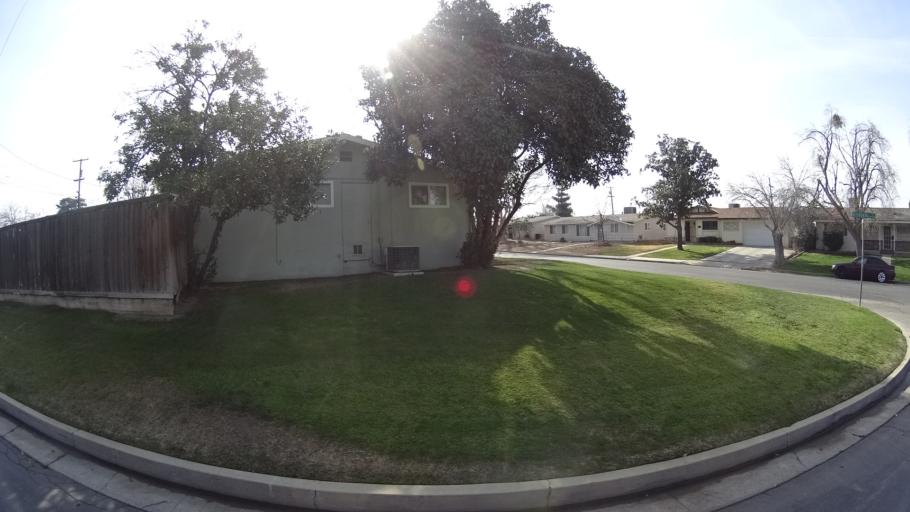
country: US
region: California
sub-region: Kern County
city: Oildale
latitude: 35.4026
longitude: -118.9703
